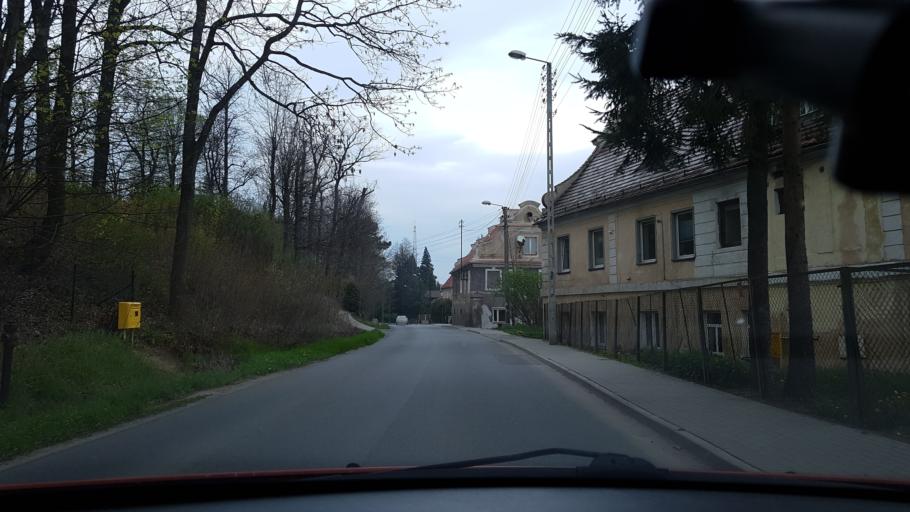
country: PL
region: Lower Silesian Voivodeship
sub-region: Powiat klodzki
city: Klodzko
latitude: 50.4246
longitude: 16.6422
